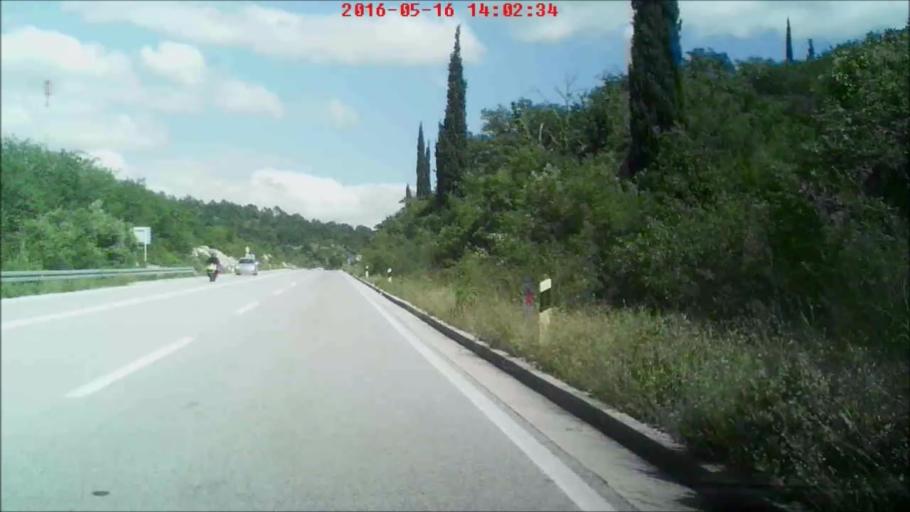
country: HR
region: Dubrovacko-Neretvanska
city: Ston
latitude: 42.8239
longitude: 17.7598
